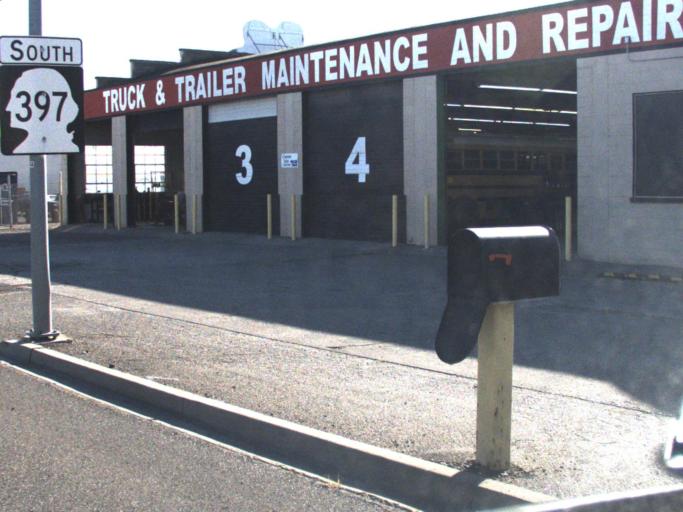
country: US
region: Washington
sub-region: Franklin County
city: Pasco
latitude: 46.2319
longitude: -119.0793
